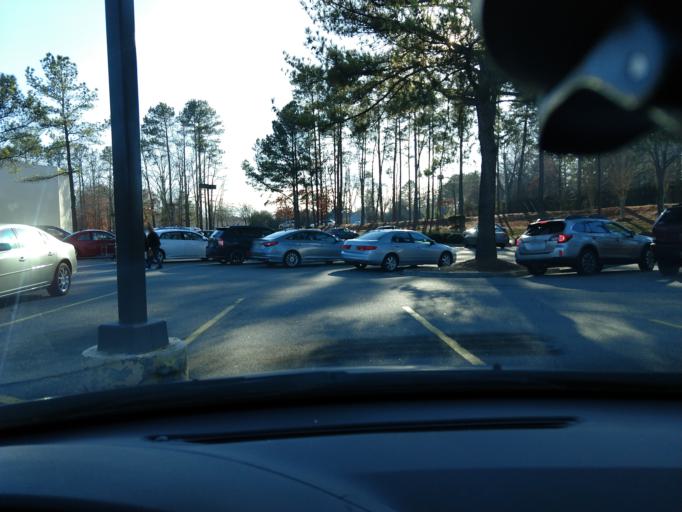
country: US
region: Virginia
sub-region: James City County
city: Williamsburg
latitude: 37.2517
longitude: -76.7647
